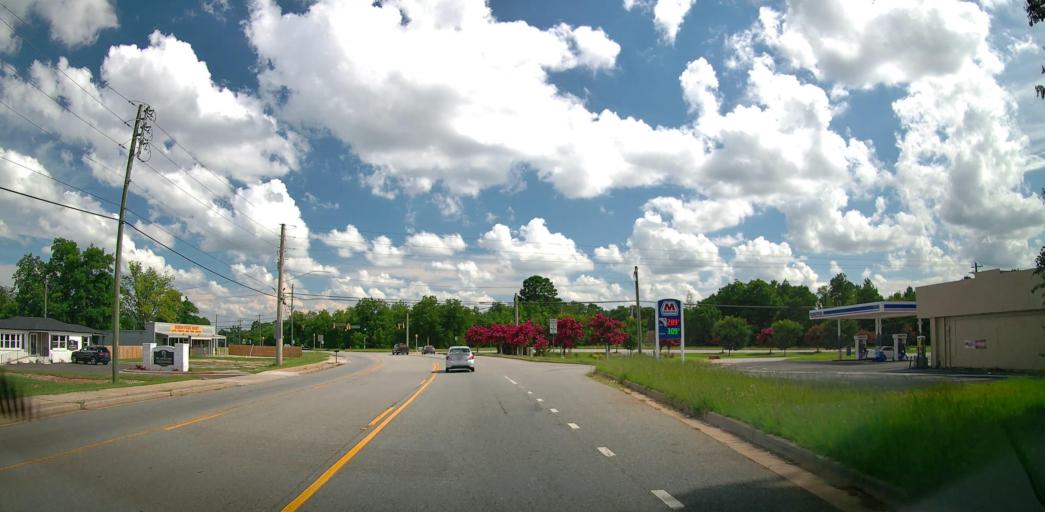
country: US
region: Georgia
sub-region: Houston County
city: Centerville
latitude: 32.6027
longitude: -83.6613
